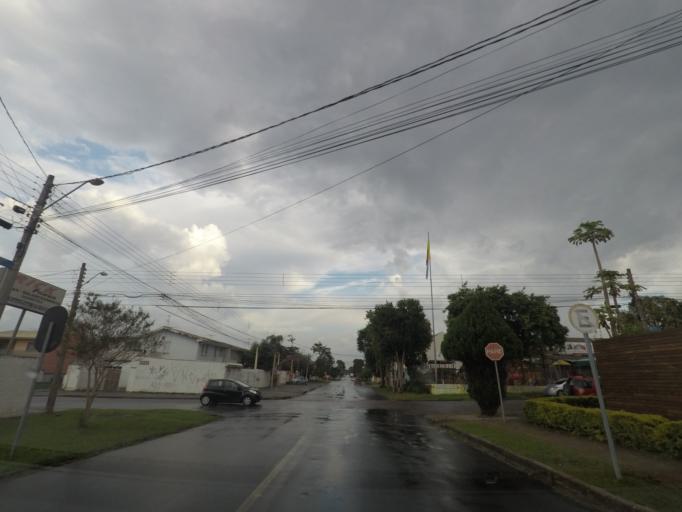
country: BR
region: Parana
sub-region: Sao Jose Dos Pinhais
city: Sao Jose dos Pinhais
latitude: -25.4863
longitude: -49.2504
